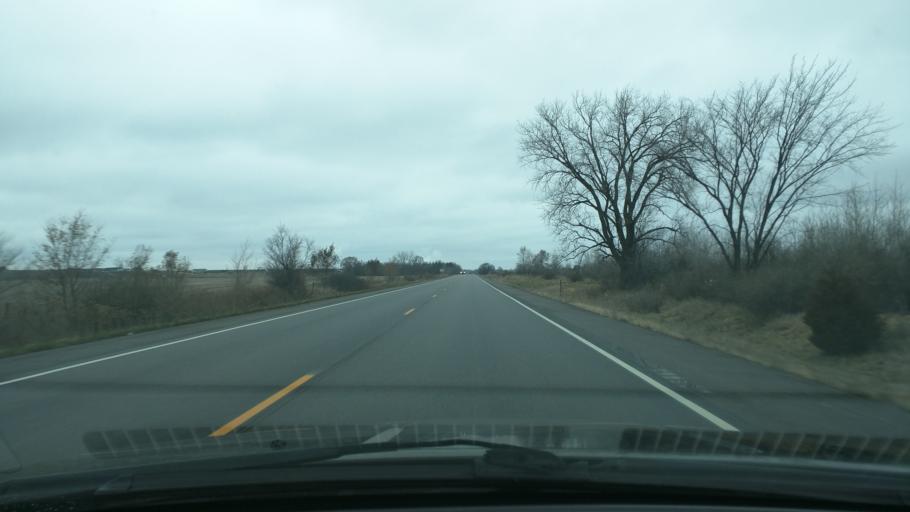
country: US
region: Minnesota
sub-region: Washington County
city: Cottage Grove
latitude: 44.7467
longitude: -92.9940
